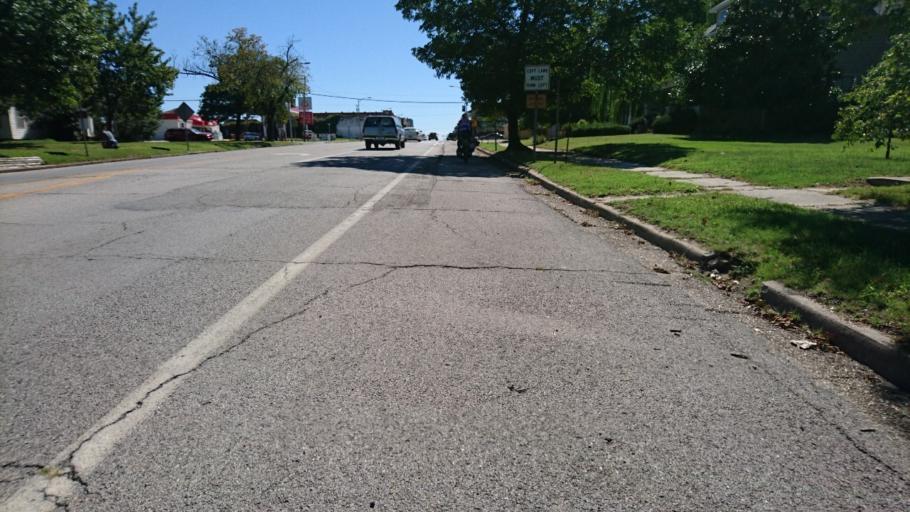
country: US
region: Kansas
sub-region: Cherokee County
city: Baxter Springs
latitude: 37.0275
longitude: -94.7351
